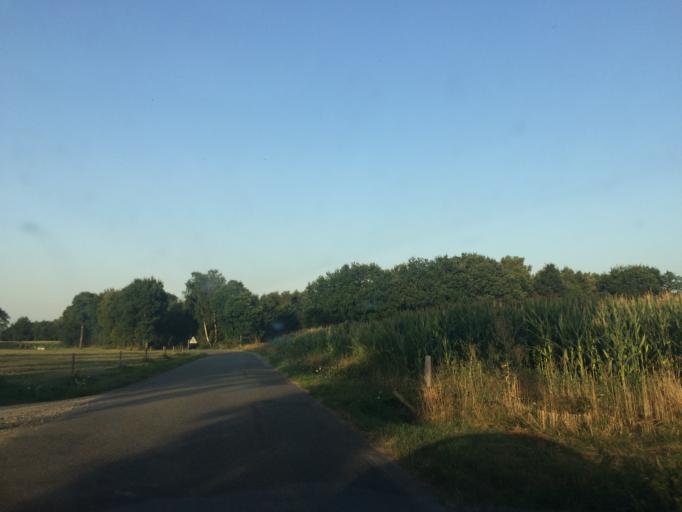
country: FR
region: Brittany
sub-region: Departement du Morbihan
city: Beganne
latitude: 47.6362
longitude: -2.2355
